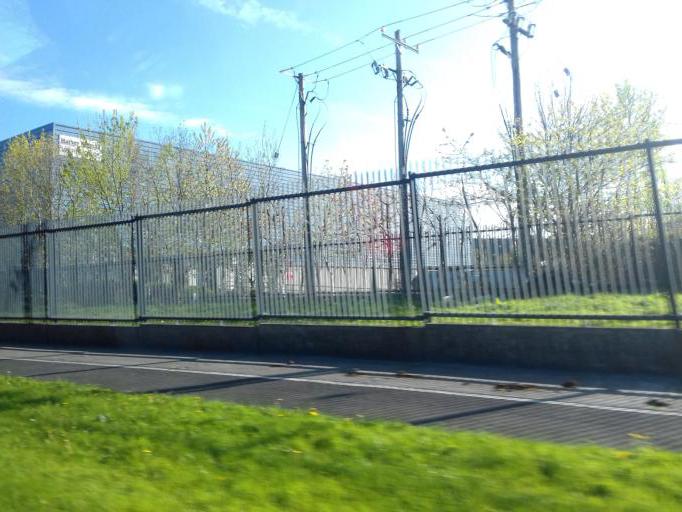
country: IE
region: Leinster
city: Castleknock
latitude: 53.4015
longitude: -6.3361
